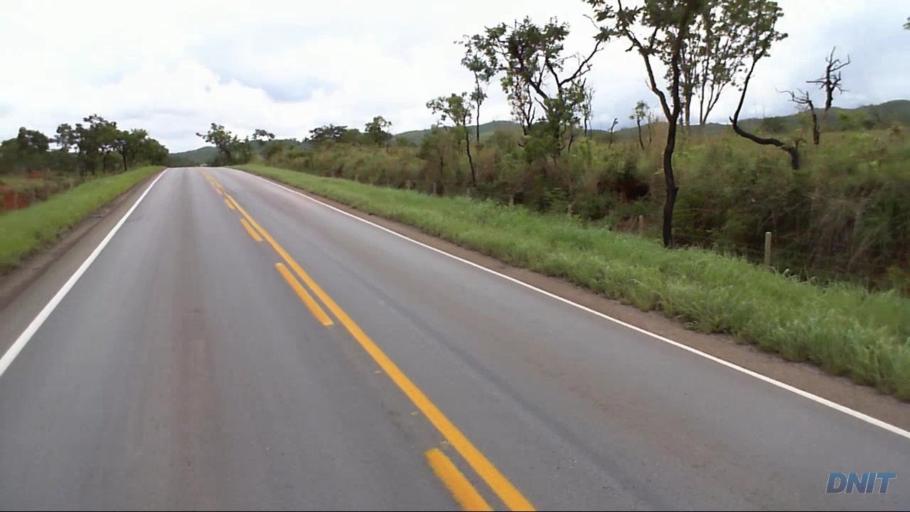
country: BR
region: Goias
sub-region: Padre Bernardo
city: Padre Bernardo
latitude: -15.4472
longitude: -48.2041
